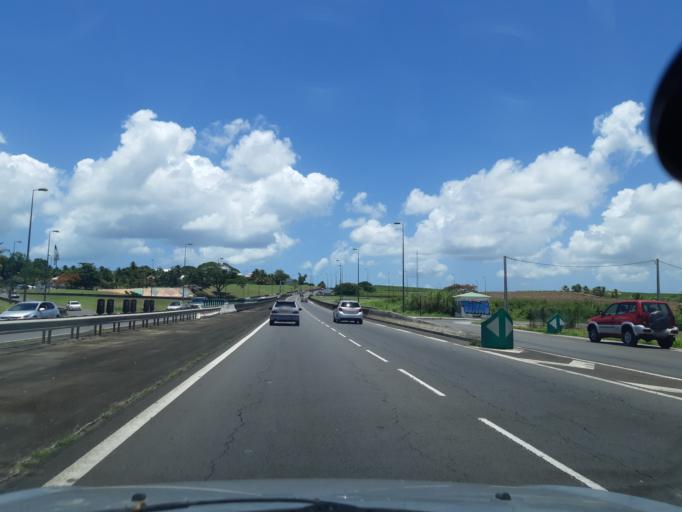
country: GP
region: Guadeloupe
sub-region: Guadeloupe
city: Petit-Bourg
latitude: 16.2154
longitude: -61.6001
